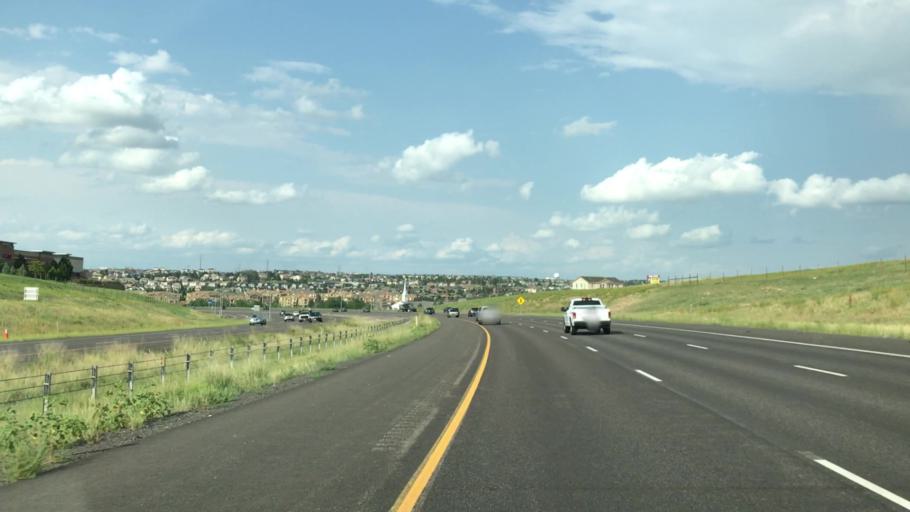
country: US
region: Colorado
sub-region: Douglas County
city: Parker
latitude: 39.5784
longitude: -104.7226
